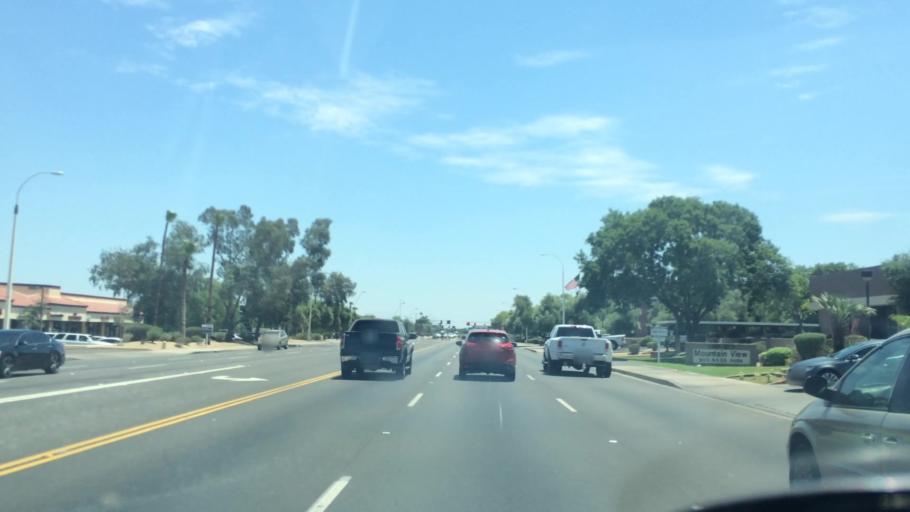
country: US
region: Arizona
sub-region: Maricopa County
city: Guadalupe
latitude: 33.3807
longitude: -111.9816
